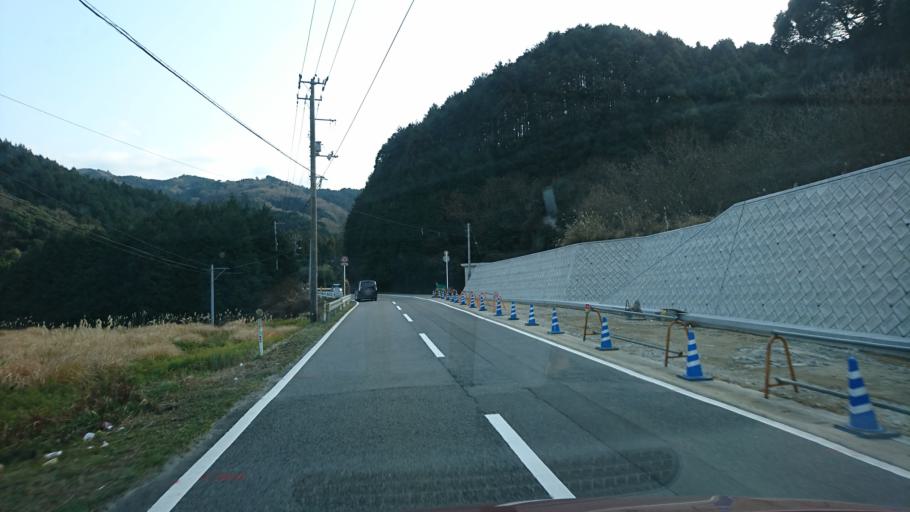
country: JP
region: Ehime
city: Hojo
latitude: 33.9854
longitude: 132.9082
